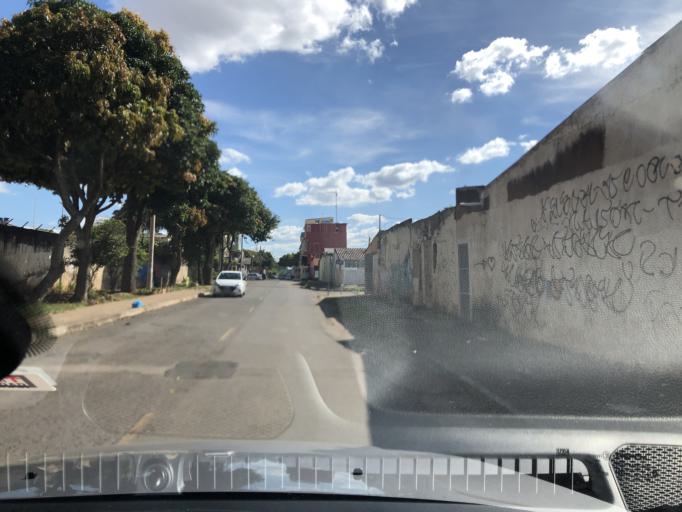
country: BR
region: Federal District
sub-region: Brasilia
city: Brasilia
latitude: -15.7954
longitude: -48.1191
